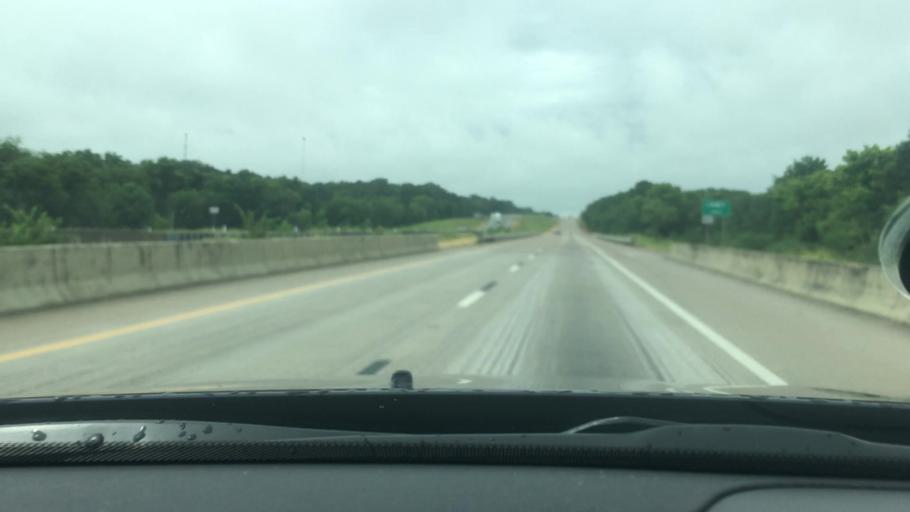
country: US
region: Oklahoma
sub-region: Atoka County
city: Atoka
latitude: 34.2431
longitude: -96.2187
